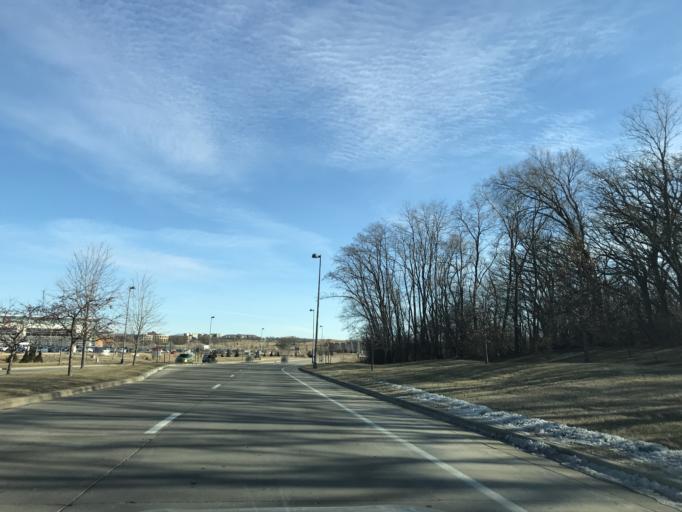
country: US
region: Wisconsin
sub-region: Dane County
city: Windsor
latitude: 43.1537
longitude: -89.3040
